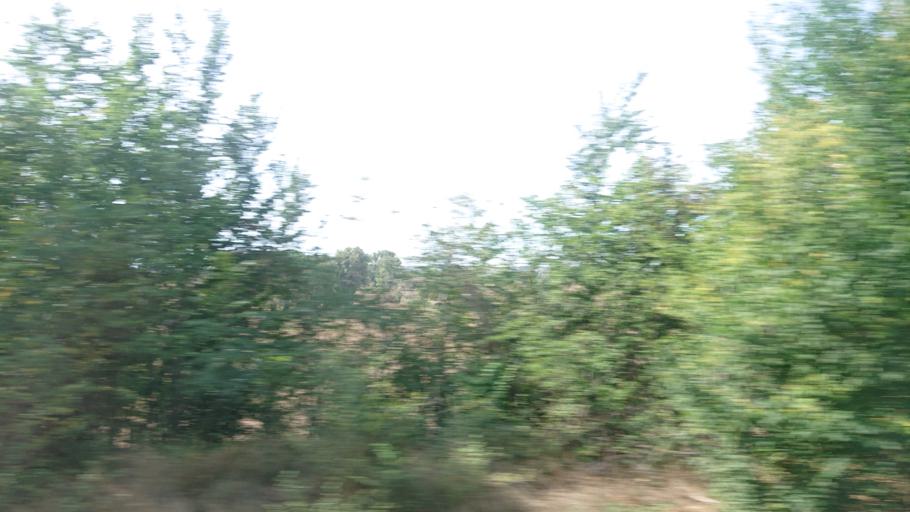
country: DE
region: Brandenburg
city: Prenzlau
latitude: 53.2963
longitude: 13.8928
